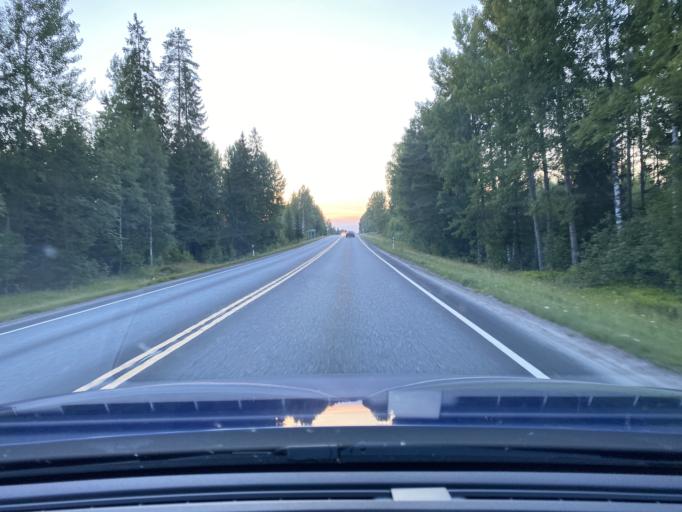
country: FI
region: Pirkanmaa
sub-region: Luoteis-Pirkanmaa
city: Ikaalinen
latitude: 61.7906
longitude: 22.9883
